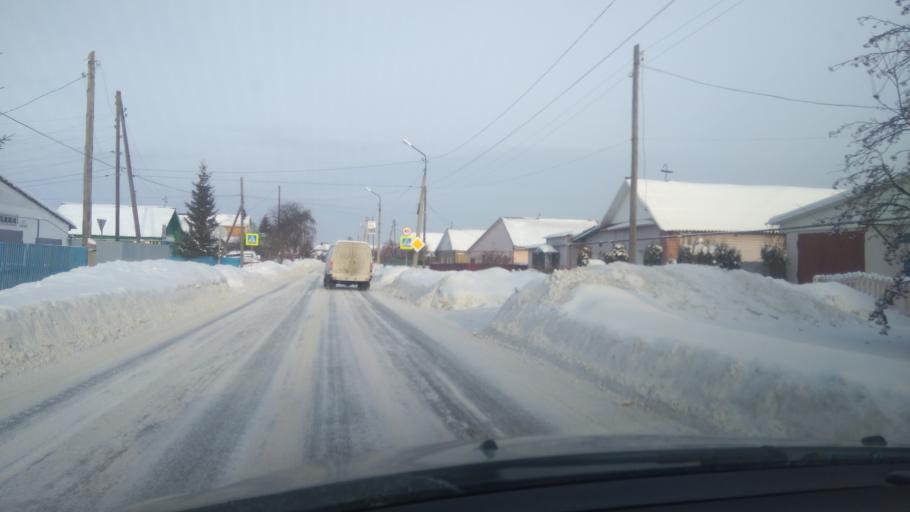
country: RU
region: Sverdlovsk
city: Sukhoy Log
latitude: 56.9044
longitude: 62.0239
